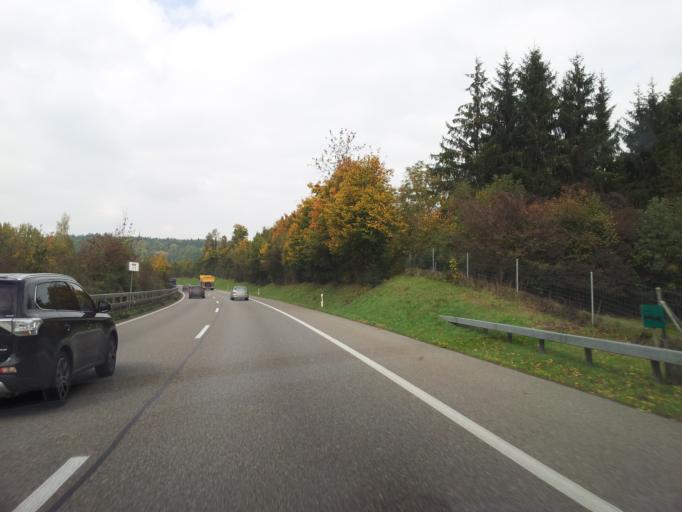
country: CH
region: Bern
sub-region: Bern-Mittelland District
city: Rubigen
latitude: 46.9011
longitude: 7.5322
